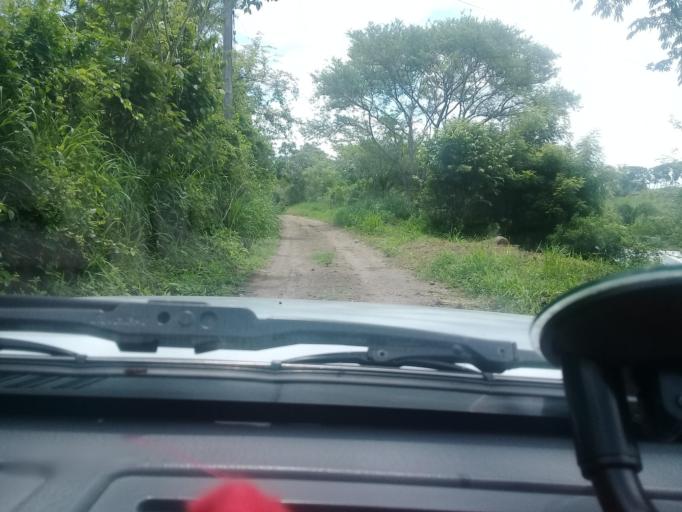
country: MX
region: Veracruz
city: Paso de Ovejas
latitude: 19.2819
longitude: -96.4279
